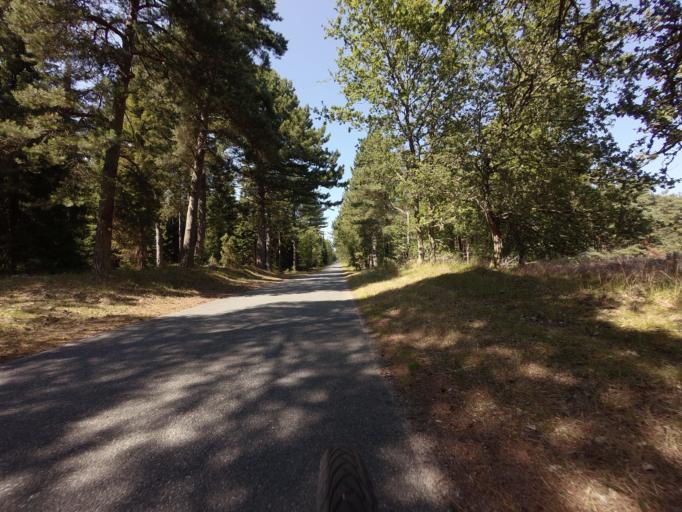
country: DK
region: North Denmark
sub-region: Laeso Kommune
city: Byrum
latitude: 57.2825
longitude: 11.0082
